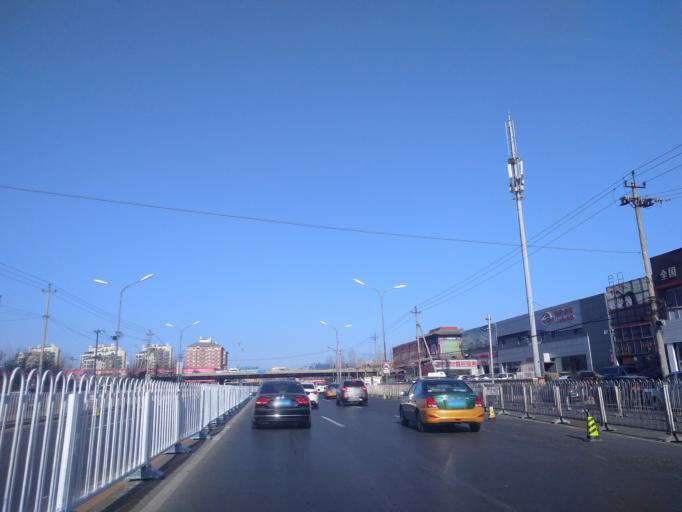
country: CN
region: Beijing
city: Jiugong
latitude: 39.8361
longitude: 116.4679
